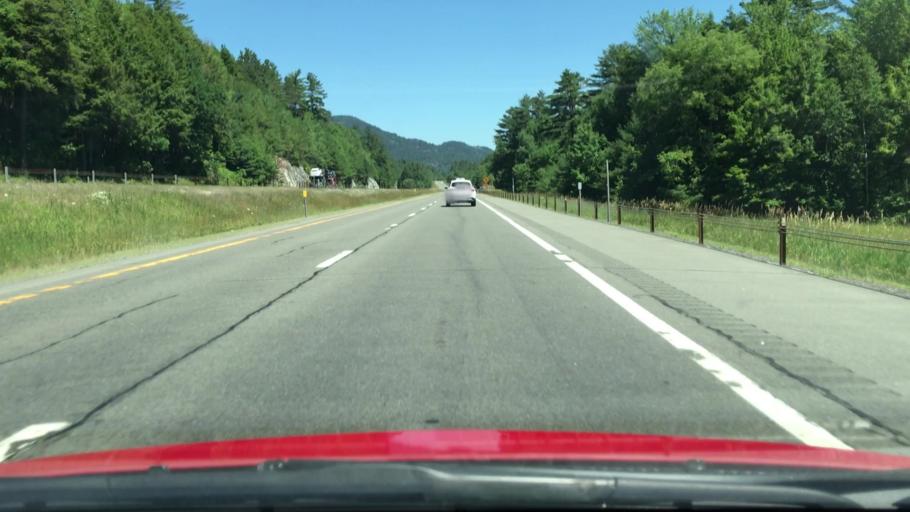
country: US
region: New York
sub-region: Essex County
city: Mineville
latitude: 43.9643
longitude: -73.7272
